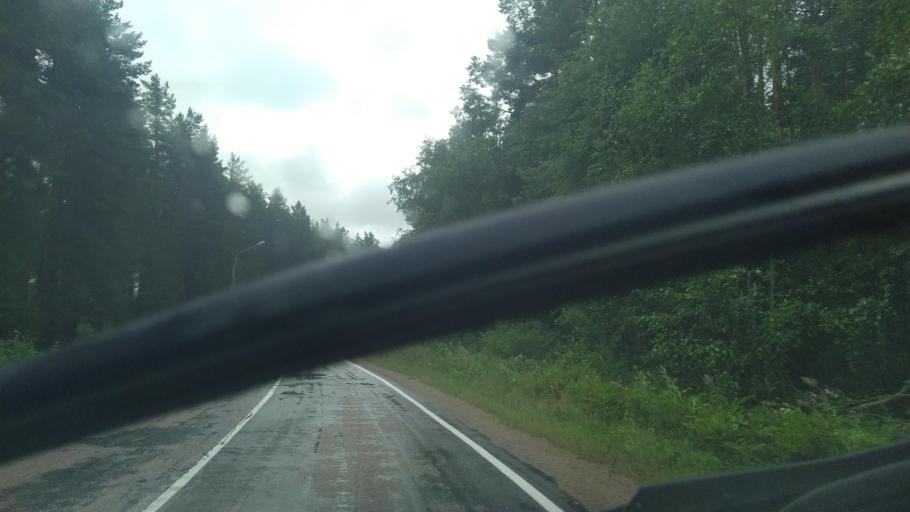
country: RU
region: Leningrad
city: Priozersk
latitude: 60.9681
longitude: 30.2857
